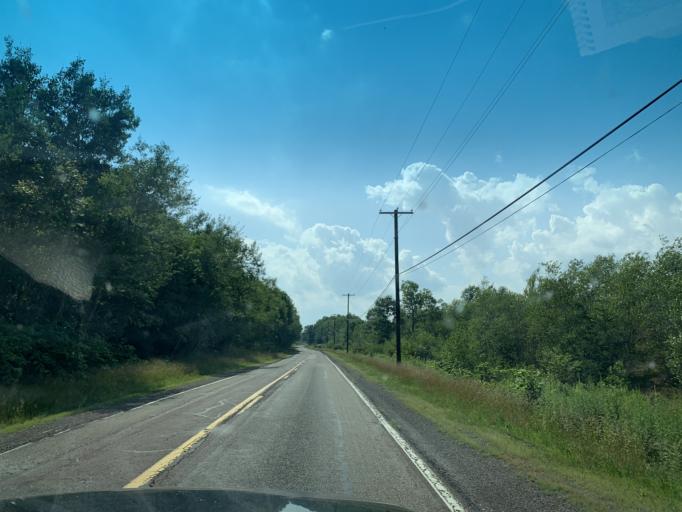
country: US
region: Pennsylvania
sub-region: Schuylkill County
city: Ashland
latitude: 40.8046
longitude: -76.3287
